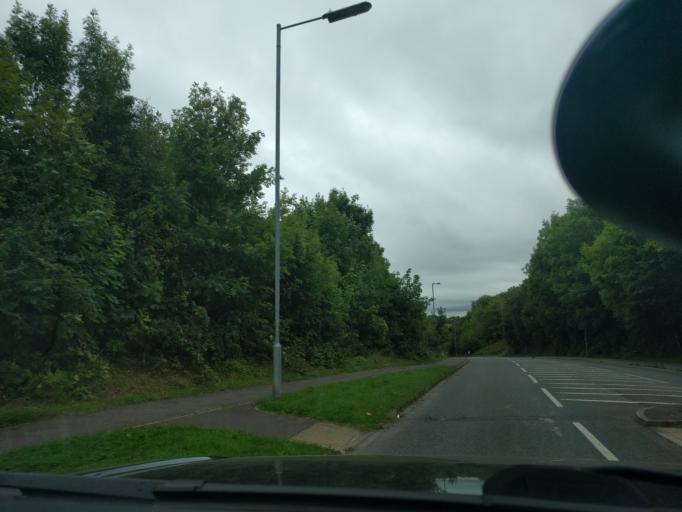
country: GB
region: England
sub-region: Wiltshire
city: Corsham
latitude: 51.4273
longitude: -2.1941
